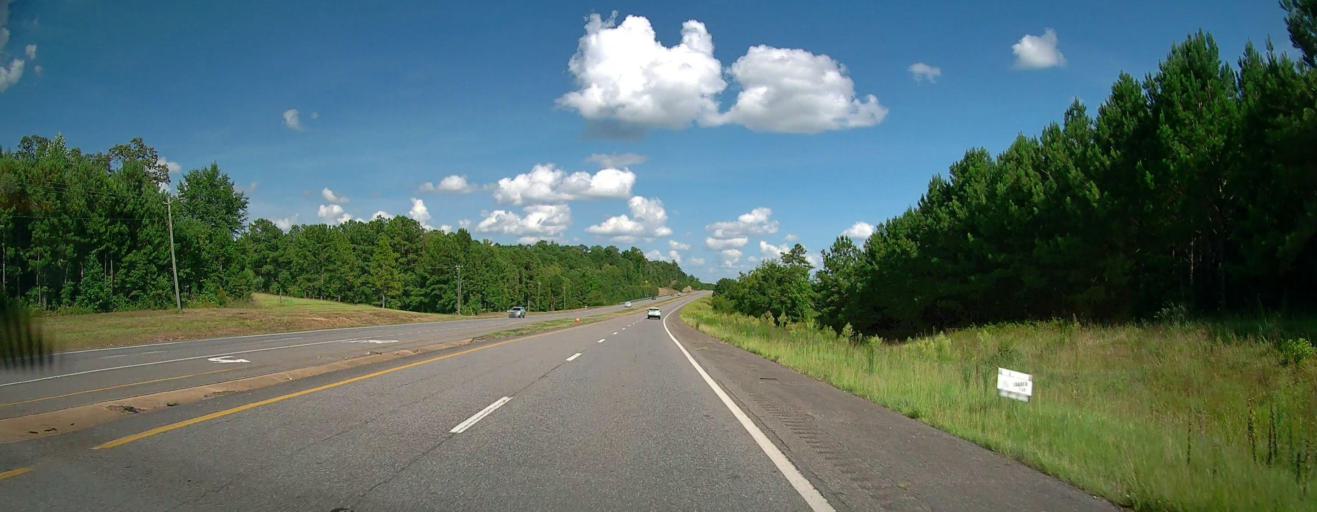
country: US
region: Alabama
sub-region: Tuscaloosa County
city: Northport
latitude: 33.2666
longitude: -87.7177
